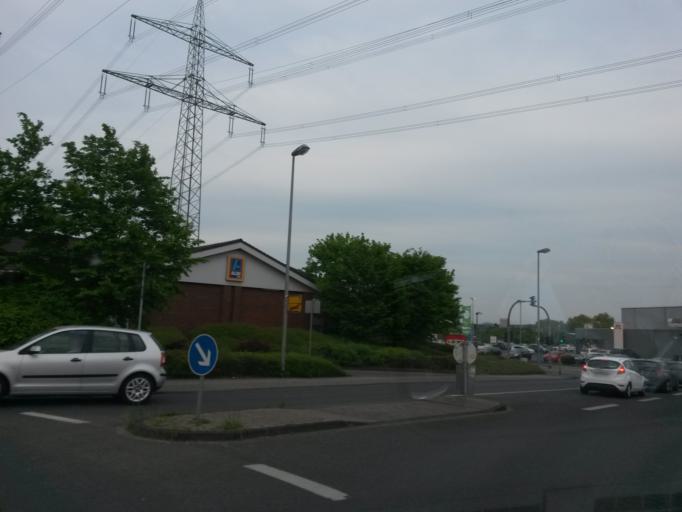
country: DE
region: North Rhine-Westphalia
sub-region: Regierungsbezirk Koln
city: Alfter
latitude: 50.7164
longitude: 7.0262
